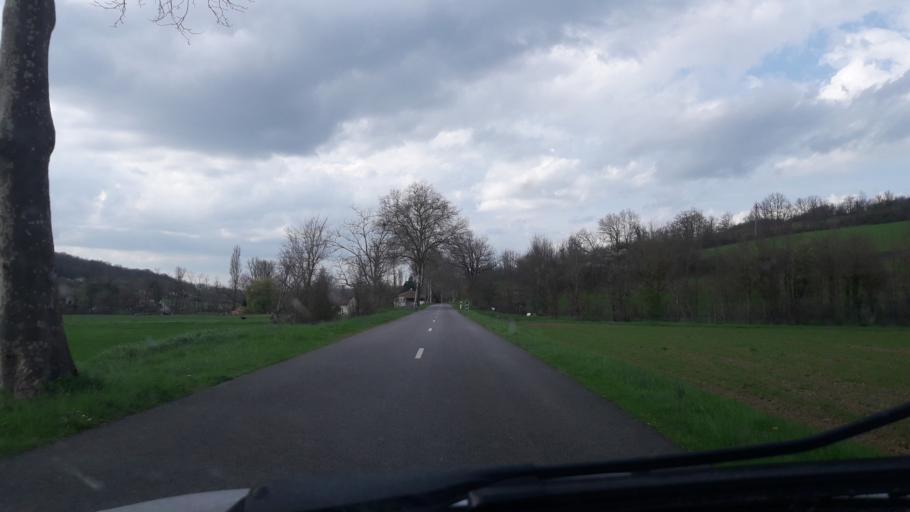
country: FR
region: Midi-Pyrenees
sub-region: Departement de la Haute-Garonne
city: Montesquieu-Volvestre
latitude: 43.2490
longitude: 1.2546
